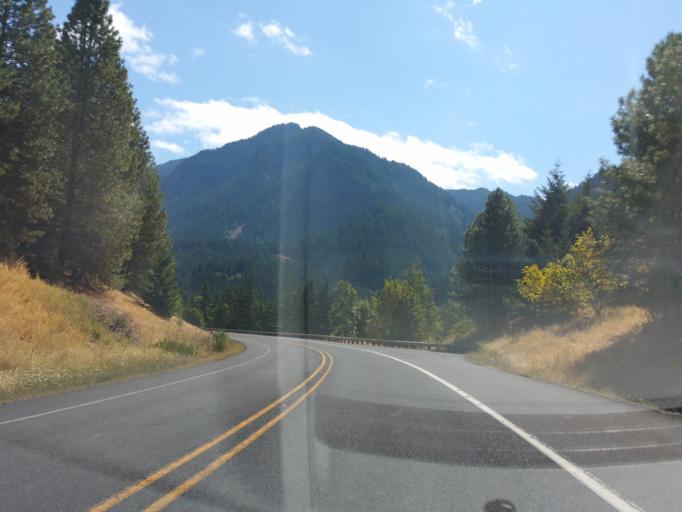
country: US
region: Oregon
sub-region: Hood River County
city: Cascade Locks
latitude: 45.6483
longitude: -121.9311
